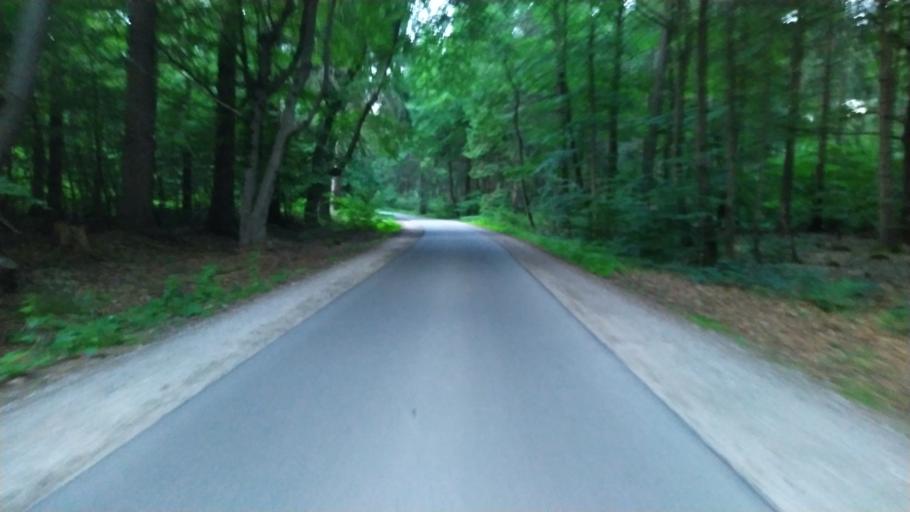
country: DE
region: Lower Saxony
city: Deinstedt
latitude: 53.4953
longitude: 9.2461
